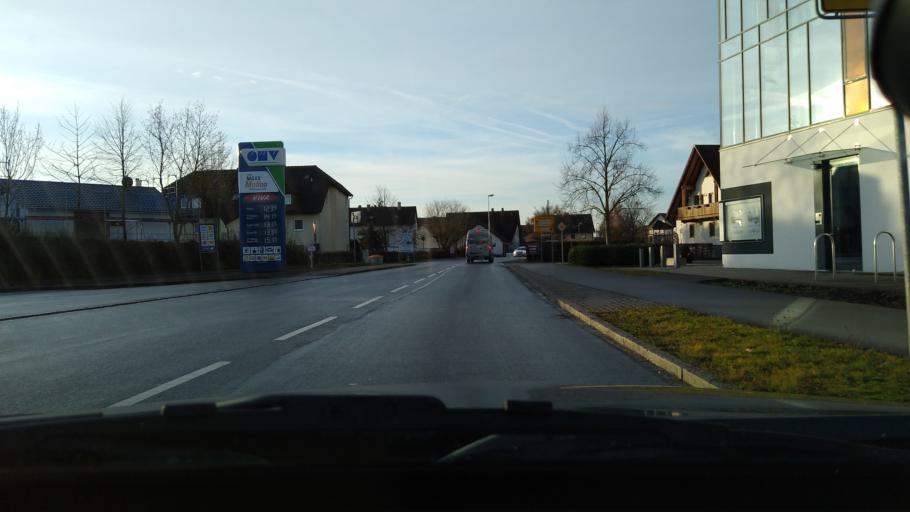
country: DE
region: Bavaria
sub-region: Regierungsbezirk Mittelfranken
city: Hessdorf
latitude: 49.6287
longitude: 10.9115
